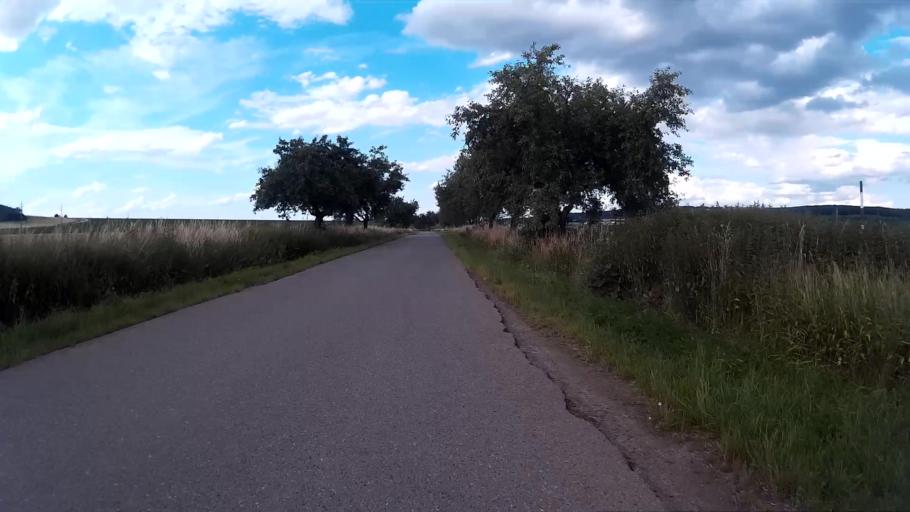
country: CZ
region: South Moravian
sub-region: Okres Brno-Venkov
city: Rosice
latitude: 49.1970
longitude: 16.3990
